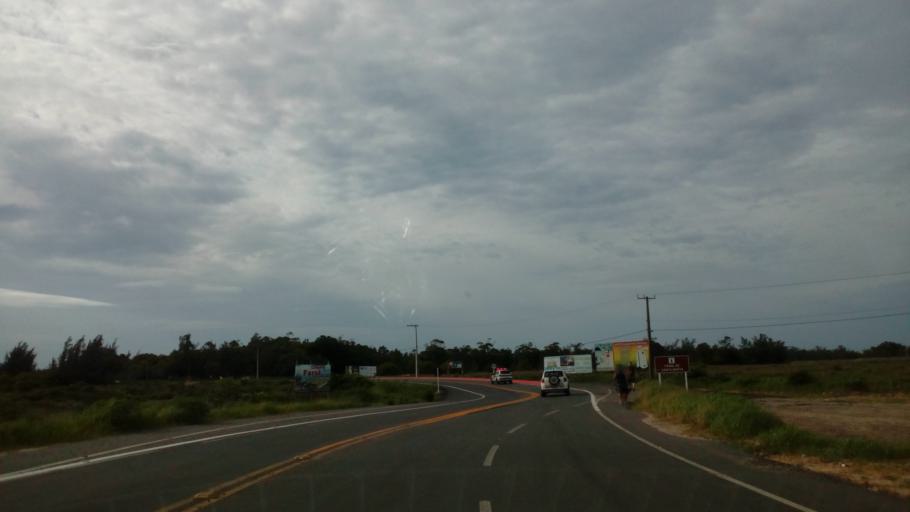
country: BR
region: Santa Catarina
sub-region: Laguna
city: Laguna
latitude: -28.5960
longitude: -48.8399
